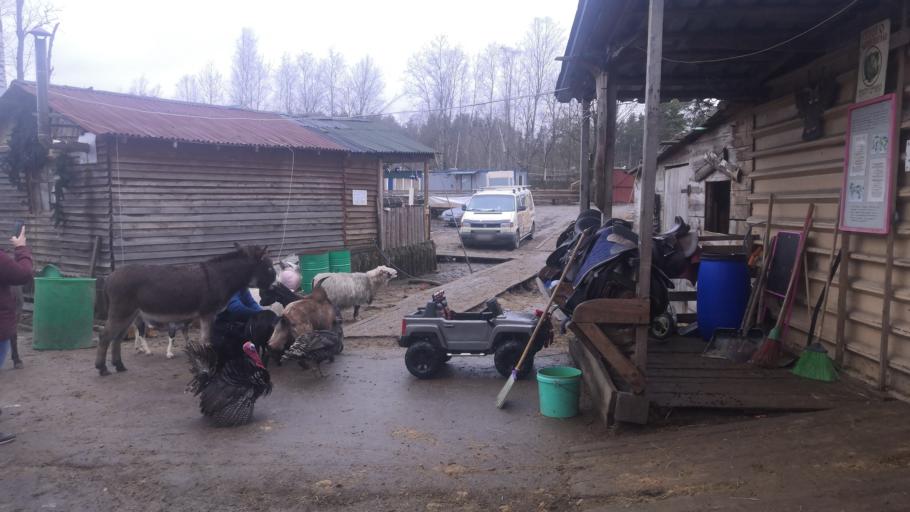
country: RU
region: Leningrad
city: Toksovo
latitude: 60.1504
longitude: 30.5046
